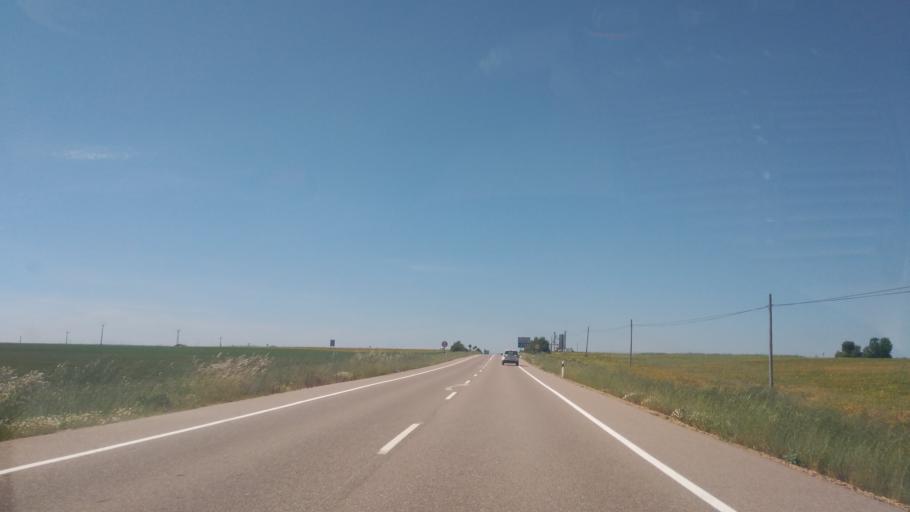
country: ES
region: Castille and Leon
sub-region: Provincia de Salamanca
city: Calzada de Valdunciel
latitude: 41.0769
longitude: -5.6927
